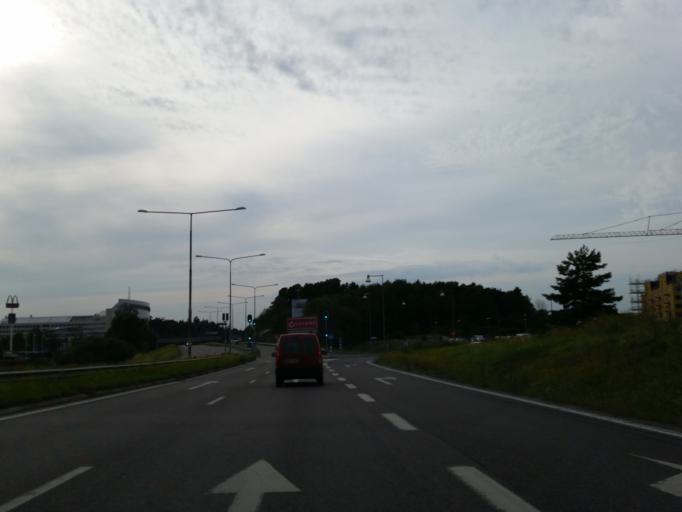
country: SE
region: Stockholm
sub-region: Stockholms Kommun
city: Kista
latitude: 59.3811
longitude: 17.9467
